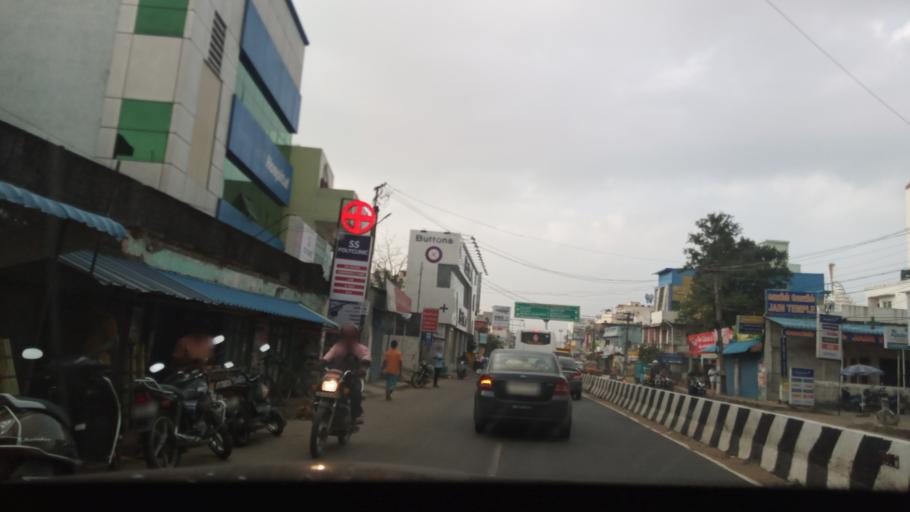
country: IN
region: Tamil Nadu
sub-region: Kancheepuram
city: Vengavasal
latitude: 12.7879
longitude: 80.2210
